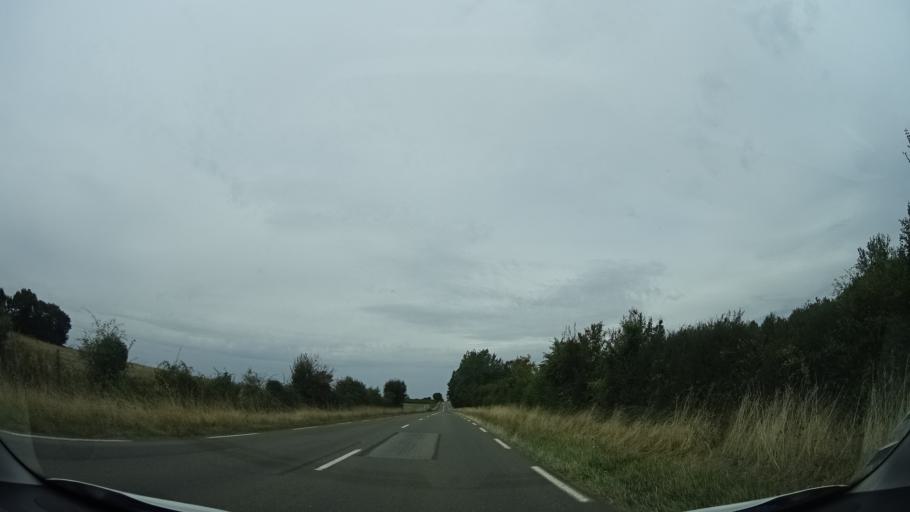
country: FR
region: Pays de la Loire
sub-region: Departement de la Mayenne
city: Meslay-du-Maine
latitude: 47.9325
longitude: -0.5002
